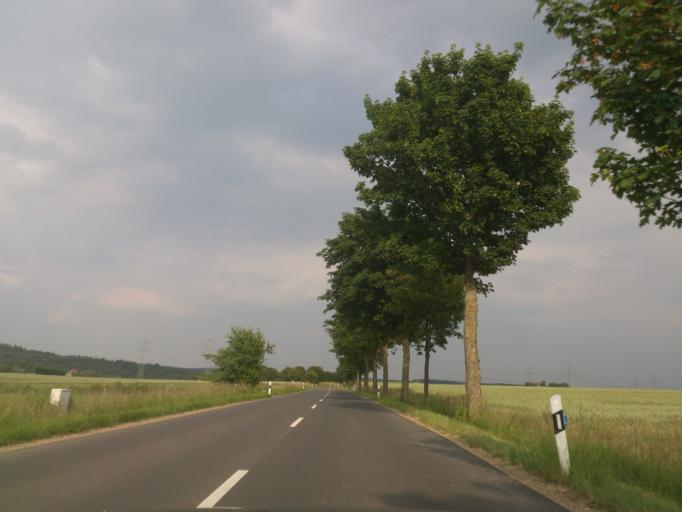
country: DE
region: North Rhine-Westphalia
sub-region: Regierungsbezirk Detmold
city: Paderborn
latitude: 51.6606
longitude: 8.7411
